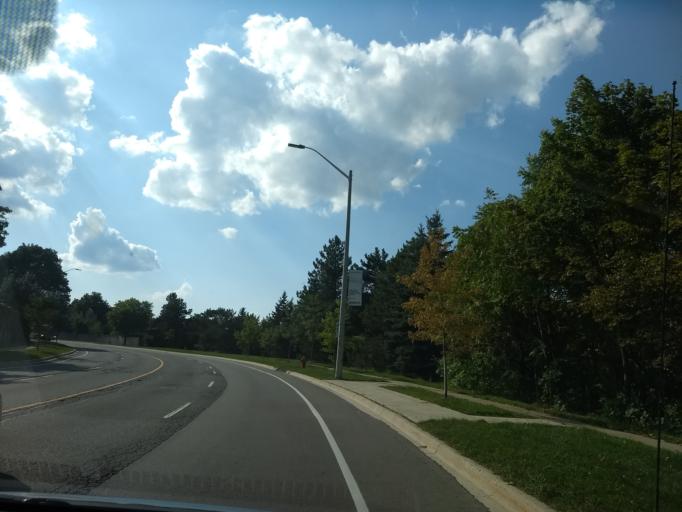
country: CA
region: Ontario
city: Mississauga
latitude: 43.5463
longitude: -79.6729
